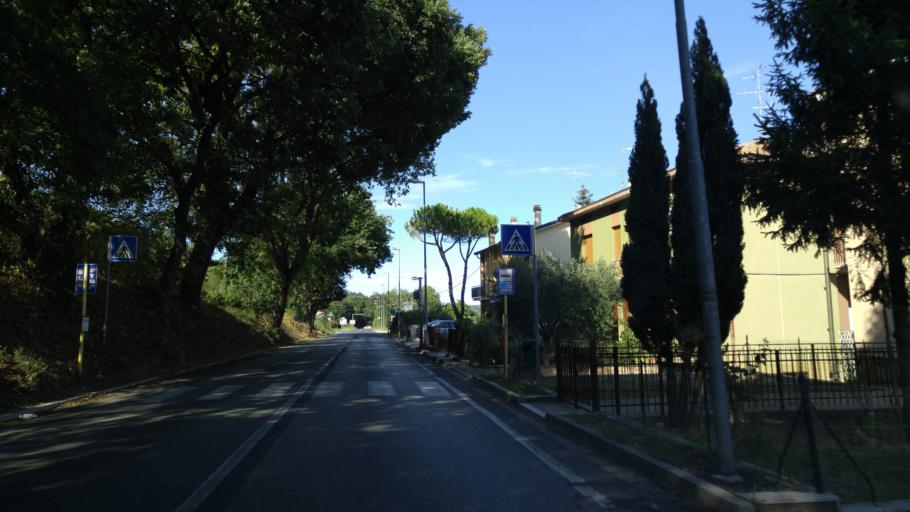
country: IT
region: The Marches
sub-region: Provincia di Pesaro e Urbino
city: Pesaro
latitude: 43.8774
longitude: 12.8954
